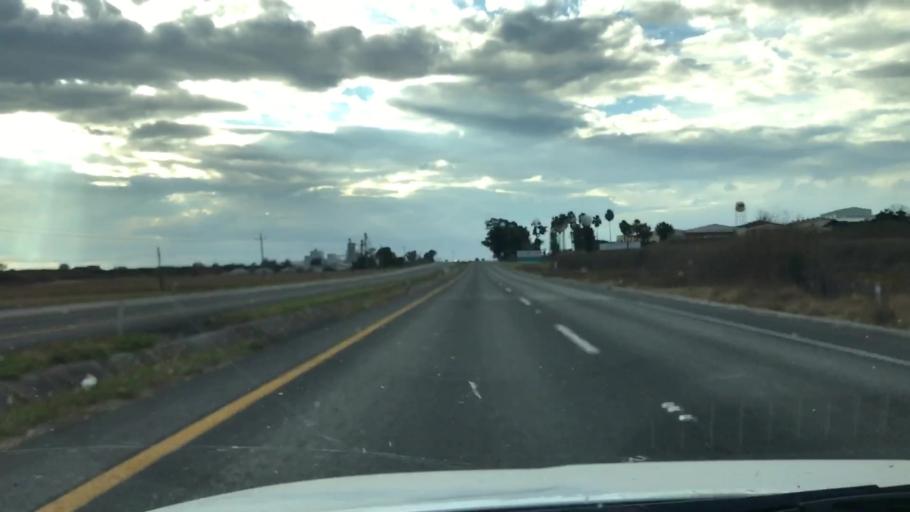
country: MX
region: Guanajuato
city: Penjamo
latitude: 20.3815
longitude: -101.8167
